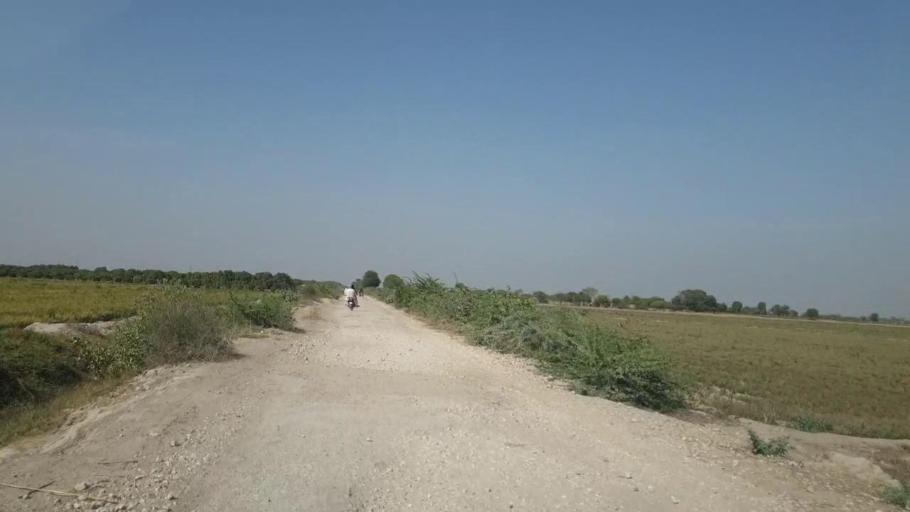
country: PK
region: Sindh
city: Nabisar
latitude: 25.0213
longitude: 69.5244
